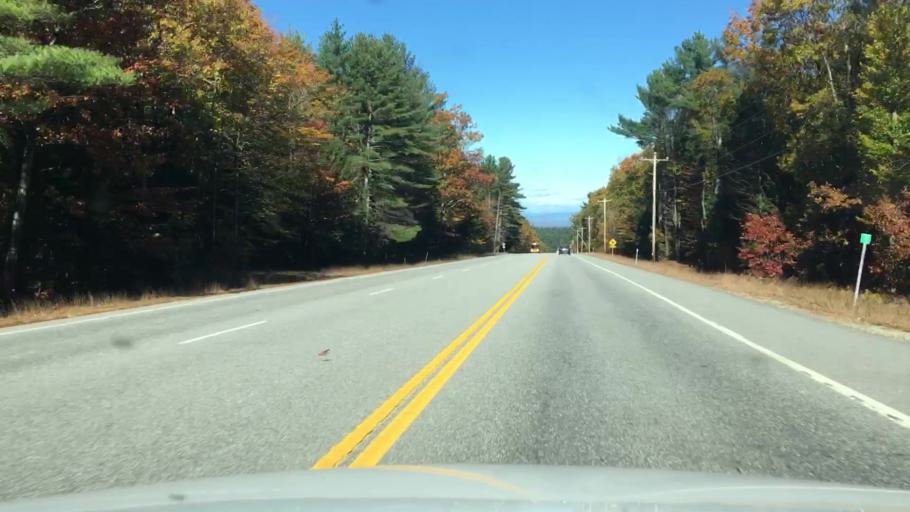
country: US
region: New Hampshire
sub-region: Carroll County
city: Wakefield
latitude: 43.6222
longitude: -71.0439
